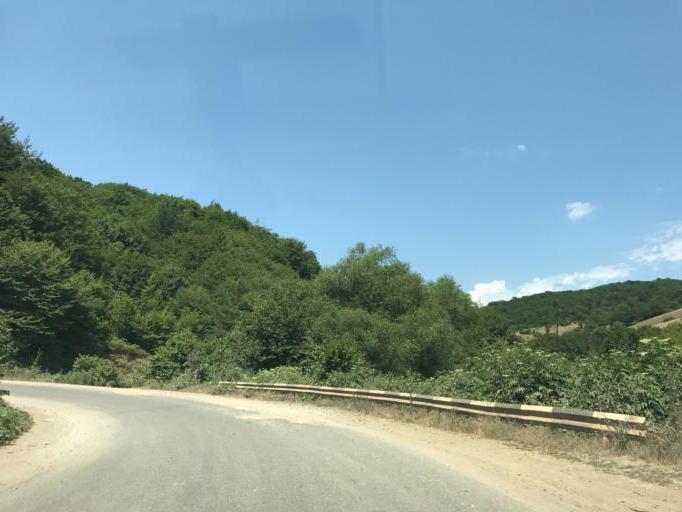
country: AZ
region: Tartar Rayon
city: Martakert
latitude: 40.1052
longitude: 46.6581
